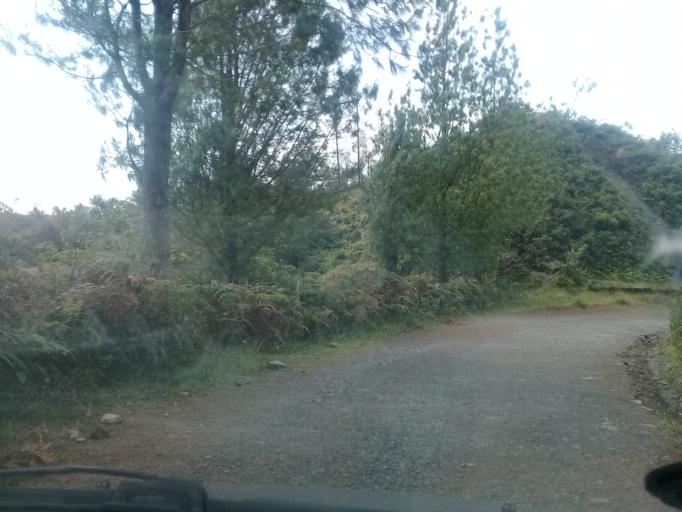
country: CO
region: Cundinamarca
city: Gachala
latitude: 4.7020
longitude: -73.4462
